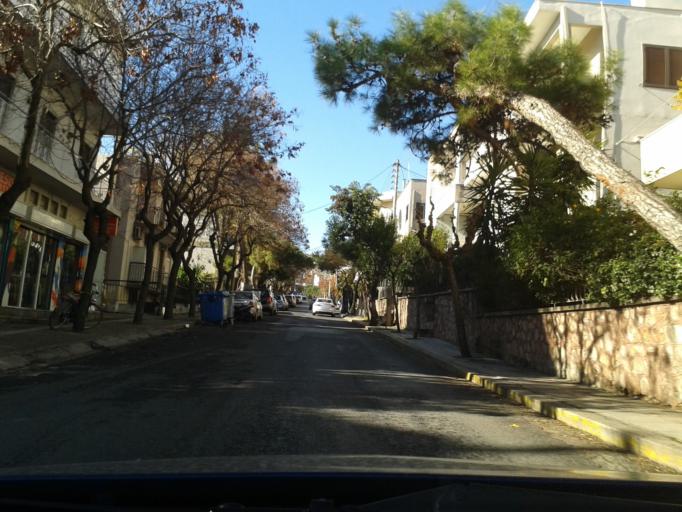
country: GR
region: Attica
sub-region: Nomarchia Athinas
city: Psychiko
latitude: 38.0012
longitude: 23.7653
